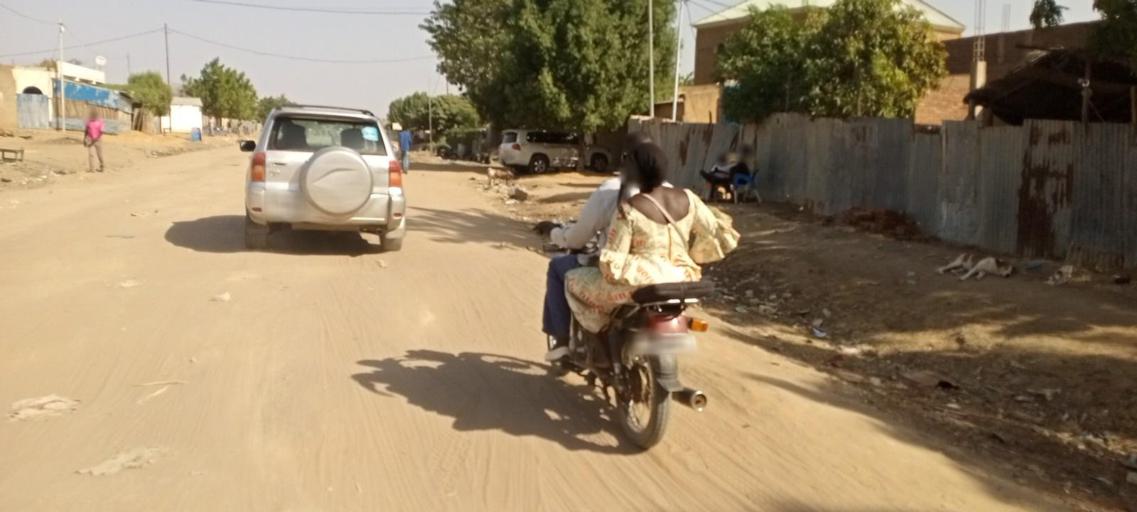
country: TD
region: Chari-Baguirmi
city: N'Djamena
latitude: 12.1129
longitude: 15.1159
